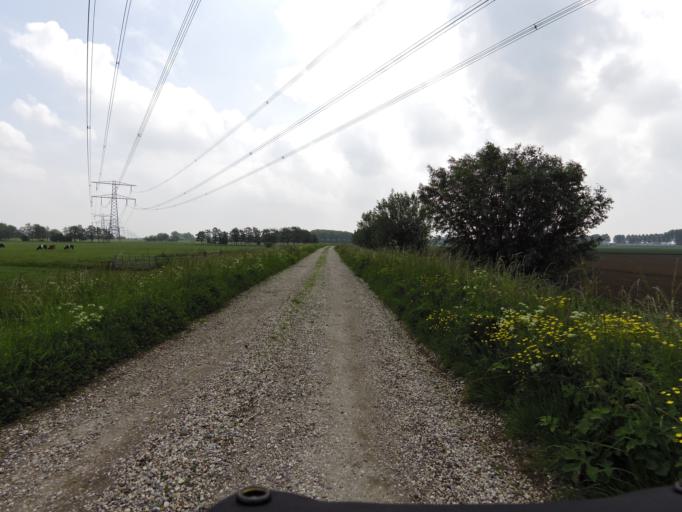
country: NL
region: South Holland
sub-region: Gemeente Spijkenisse
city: Spijkenisse
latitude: 51.8420
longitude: 4.2547
